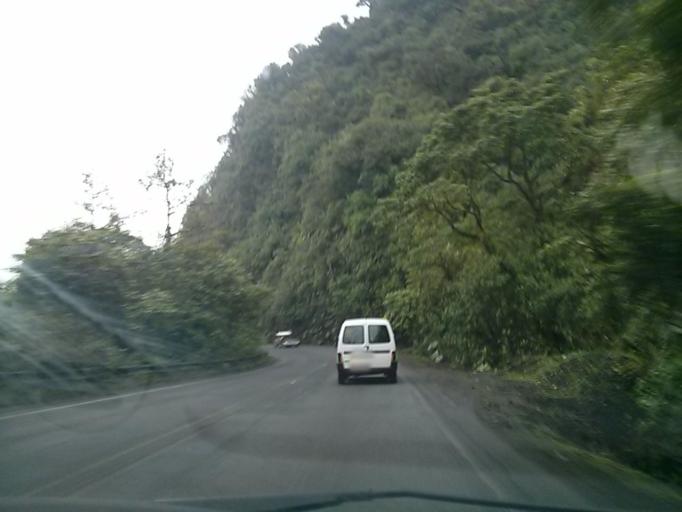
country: CR
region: San Jose
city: Dulce Nombre de Jesus
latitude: 10.0692
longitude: -83.9859
